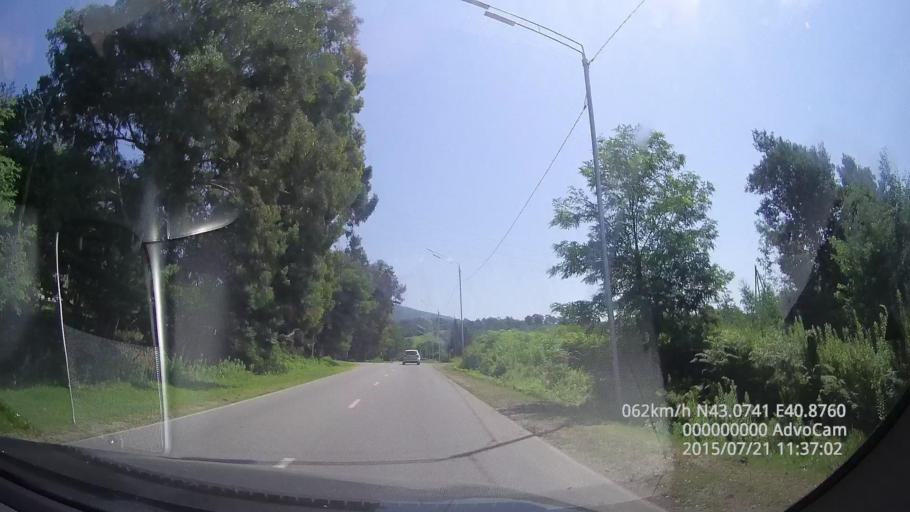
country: GE
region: Abkhazia
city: Stantsiya Novyy Afon
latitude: 43.0742
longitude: 40.8766
